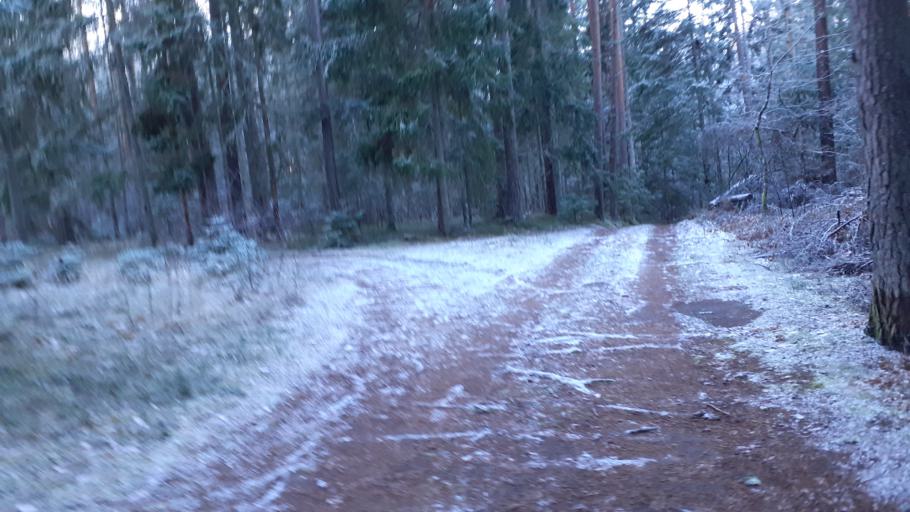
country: LV
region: Kuldigas Rajons
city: Kuldiga
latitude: 57.0103
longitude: 21.9702
